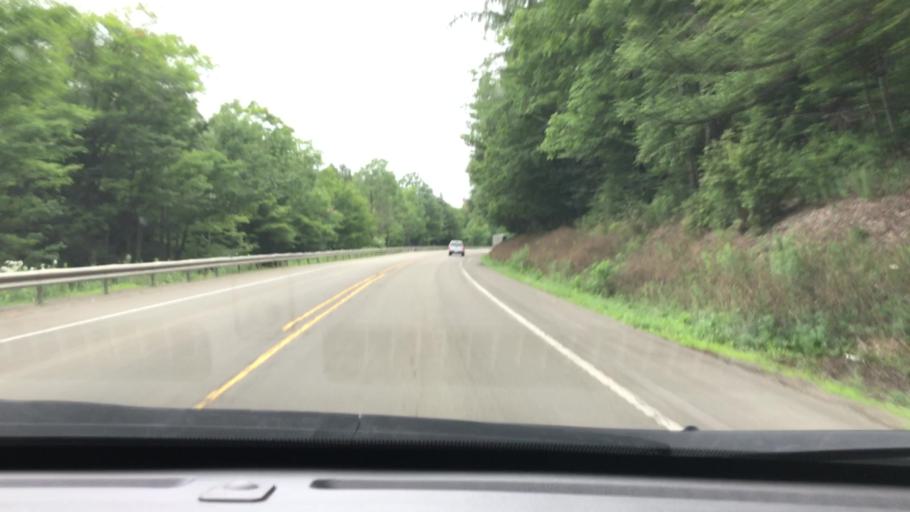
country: US
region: Pennsylvania
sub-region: McKean County
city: Kane
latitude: 41.6610
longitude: -78.6815
